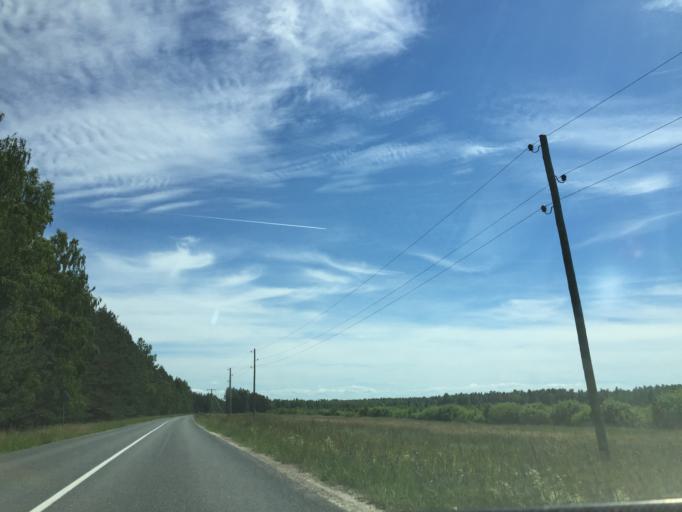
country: LV
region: Dundaga
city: Dundaga
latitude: 57.6259
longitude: 22.5775
